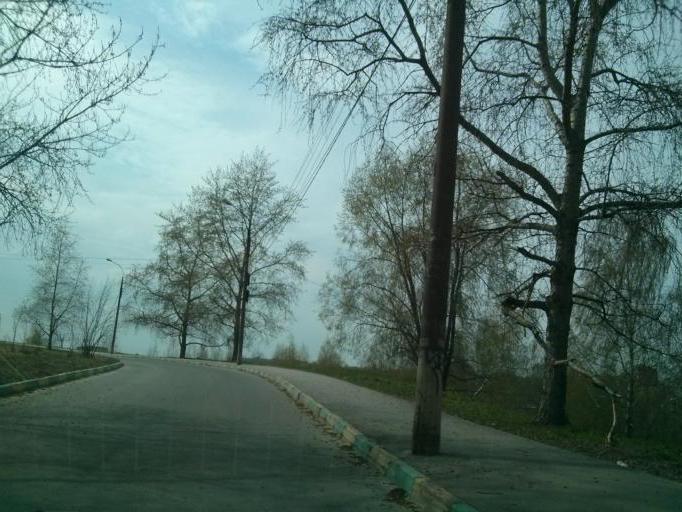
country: RU
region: Nizjnij Novgorod
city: Afonino
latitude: 56.3003
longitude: 44.0576
